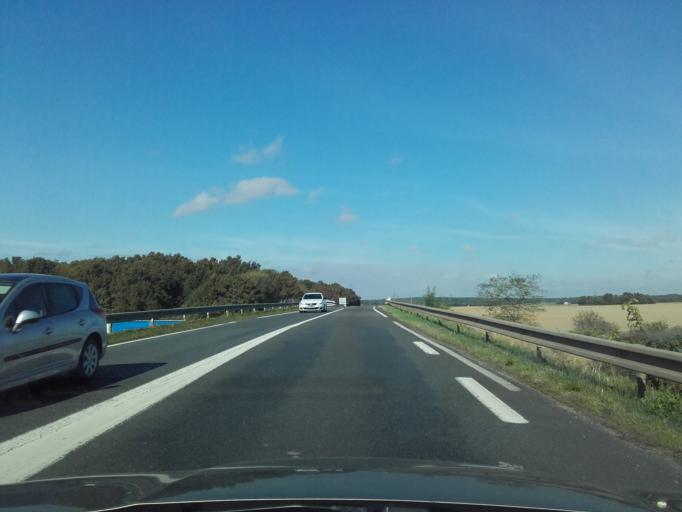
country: FR
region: Centre
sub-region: Departement d'Indre-et-Loire
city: Auzouer-en-Touraine
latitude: 47.5438
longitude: 0.9820
